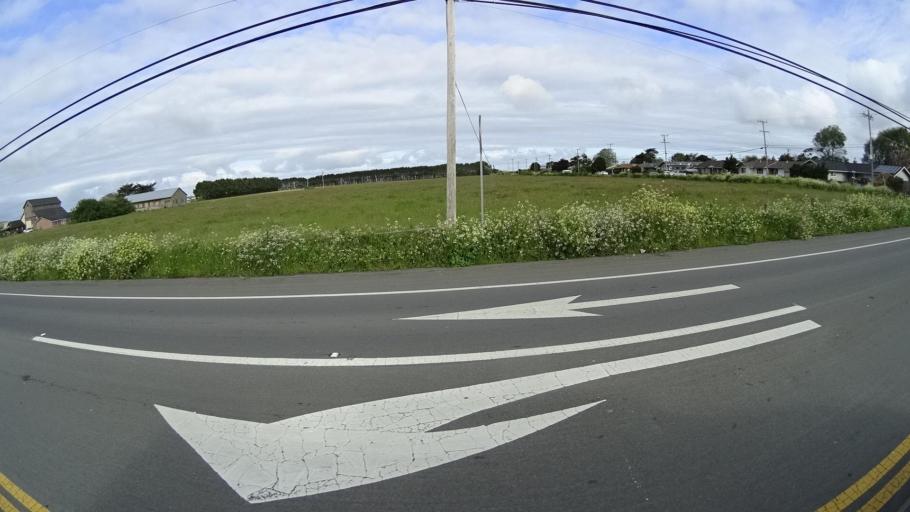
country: US
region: California
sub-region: Humboldt County
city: Arcata
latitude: 40.8943
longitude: -124.0938
